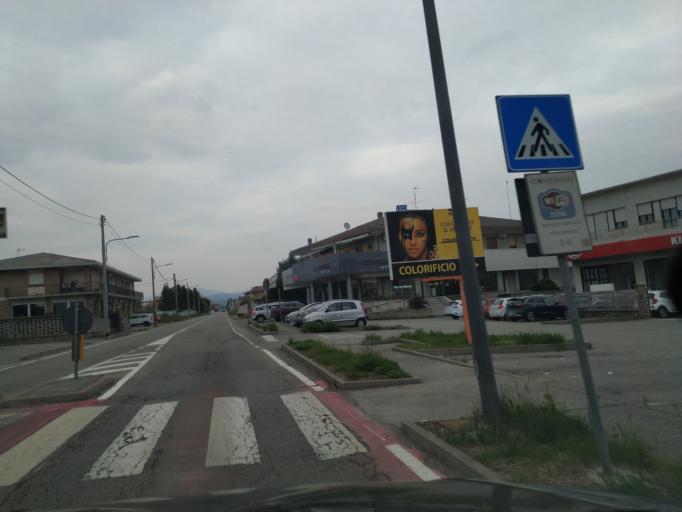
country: IT
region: Piedmont
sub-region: Provincia di Novara
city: Cureggio
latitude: 45.6780
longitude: 8.4562
